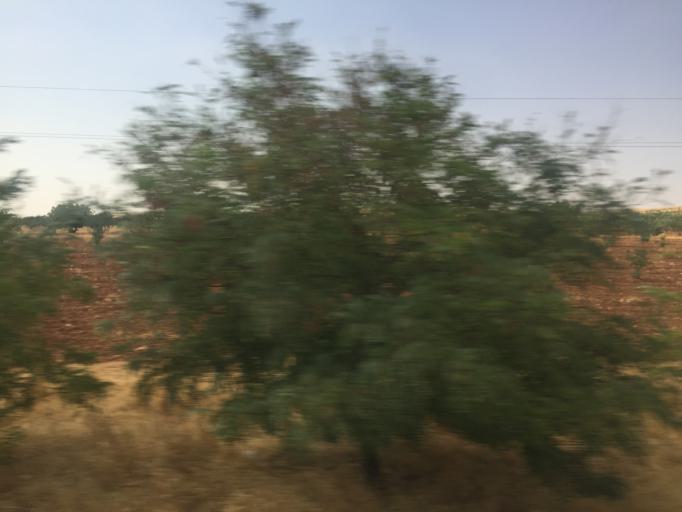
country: TR
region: Sanliurfa
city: Akziyaret
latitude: 37.3919
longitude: 38.8615
